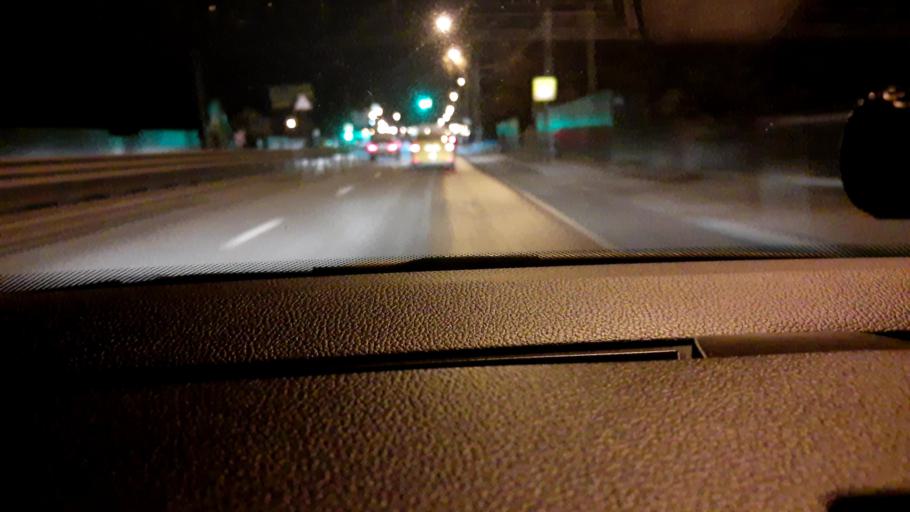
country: RU
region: Moscow
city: Vatutino
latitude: 55.9242
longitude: 37.6623
